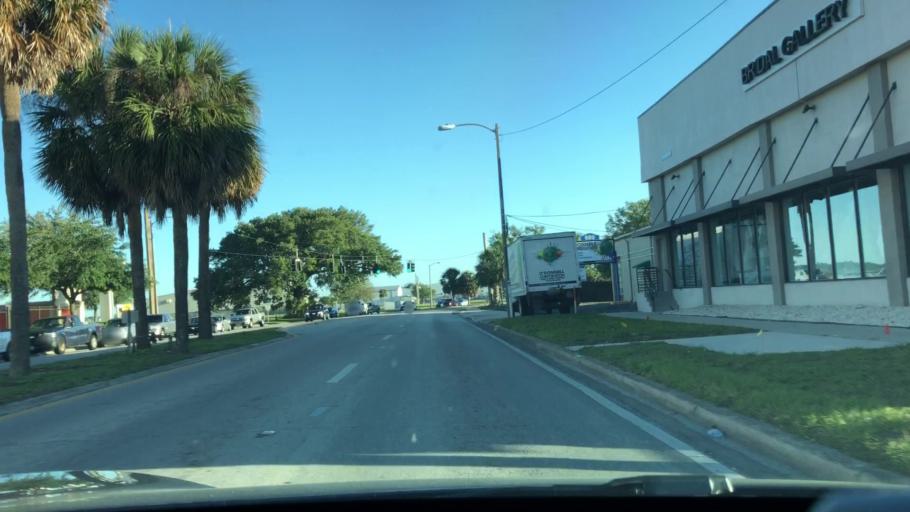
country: US
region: Florida
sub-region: Orange County
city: Orlando
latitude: 28.5523
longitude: -81.3448
